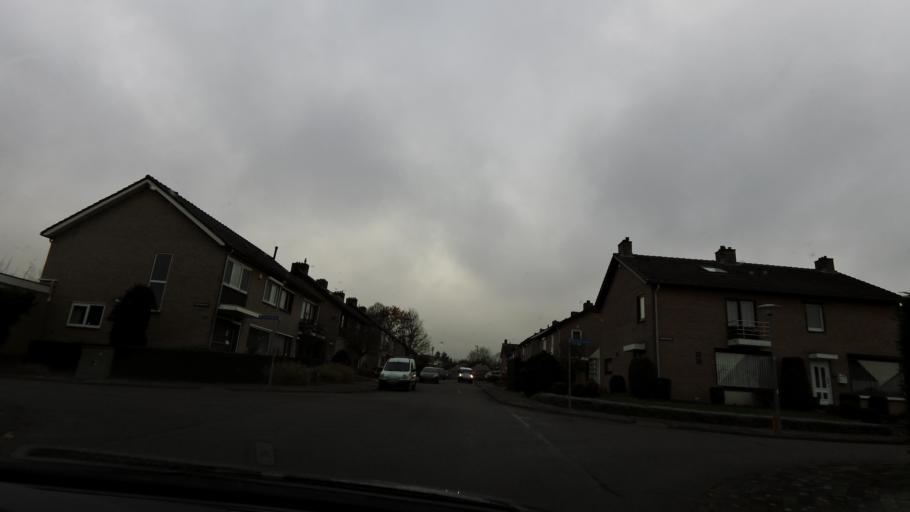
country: NL
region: Limburg
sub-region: Gemeente Voerendaal
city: Klimmen
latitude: 50.8915
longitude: 5.8618
